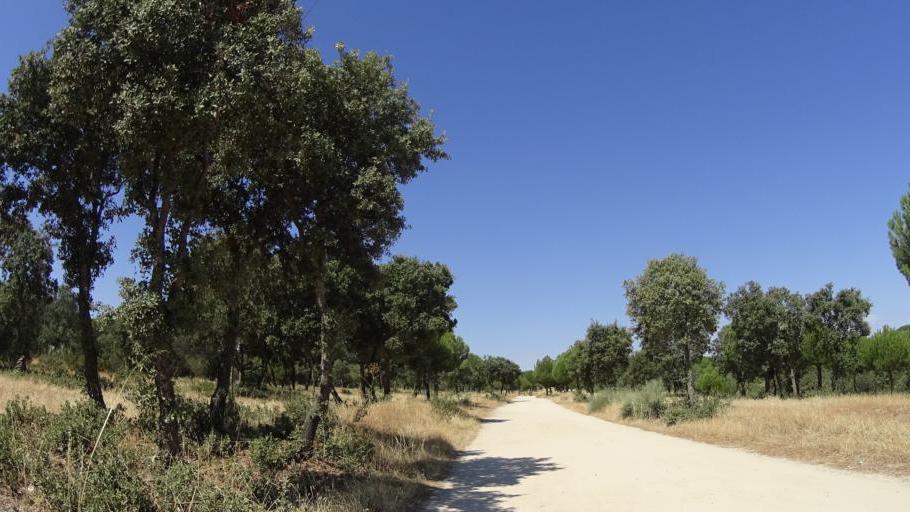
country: ES
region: Madrid
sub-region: Provincia de Madrid
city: Boadilla del Monte
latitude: 40.4337
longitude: -3.8567
